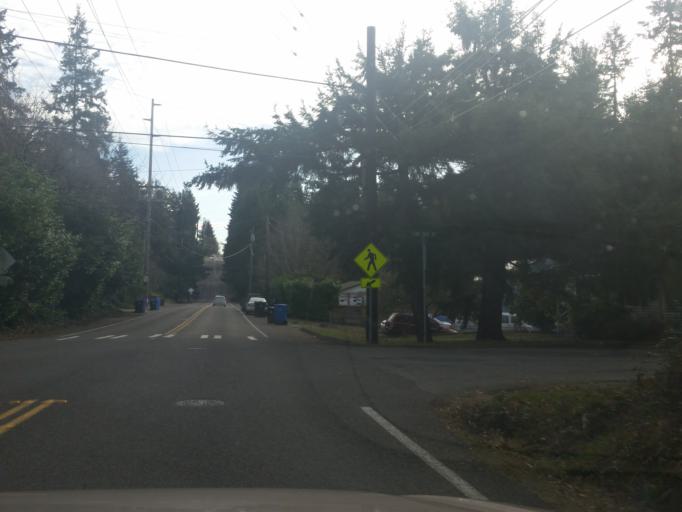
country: US
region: Washington
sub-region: King County
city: Shoreline
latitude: 47.7597
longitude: -122.3242
